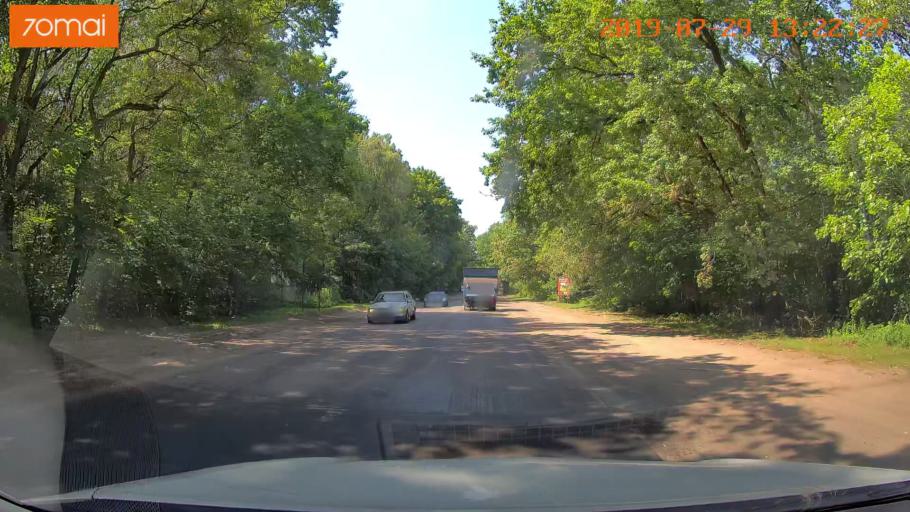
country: RU
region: Kaliningrad
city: Vzmorye
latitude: 54.7149
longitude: 20.3691
